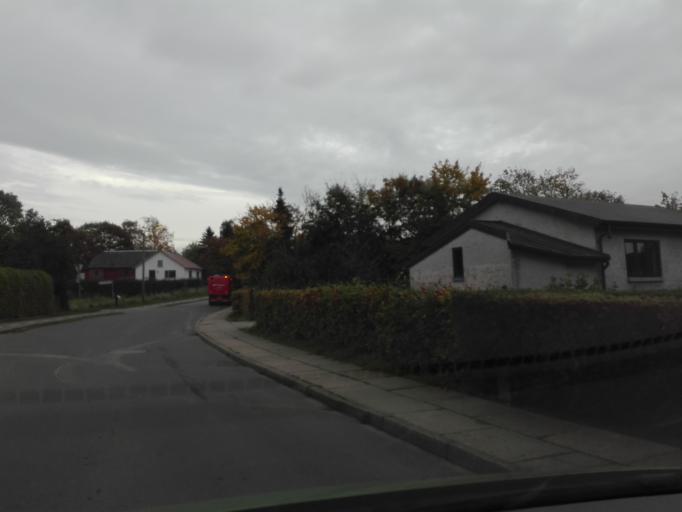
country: DK
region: Central Jutland
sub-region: Skanderborg Kommune
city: Horning
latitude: 56.0811
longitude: 10.0432
